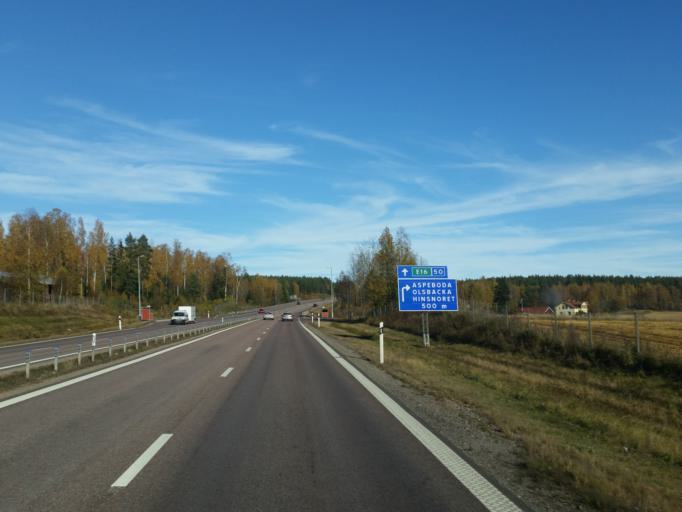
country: SE
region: Dalarna
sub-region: Borlange Kommun
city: Ornas
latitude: 60.5457
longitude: 15.5665
